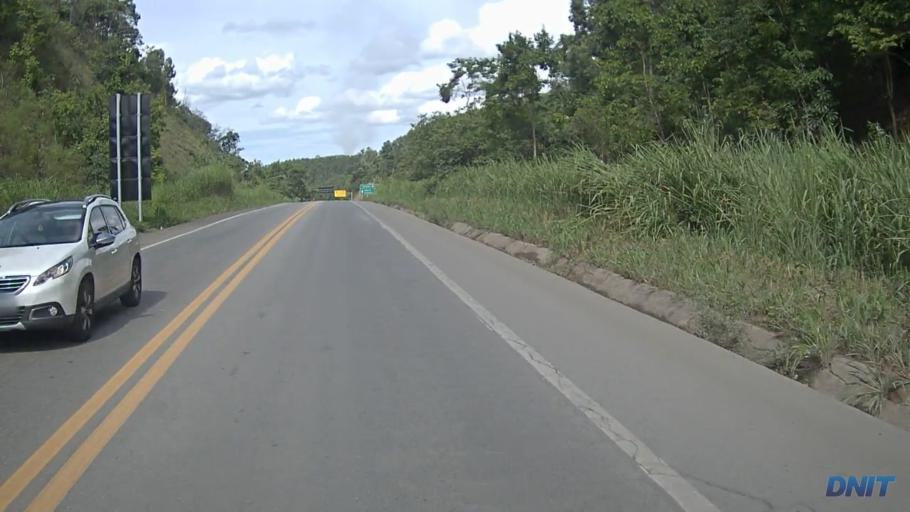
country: BR
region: Minas Gerais
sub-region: Ipaba
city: Ipaba
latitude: -19.3241
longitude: -42.4152
